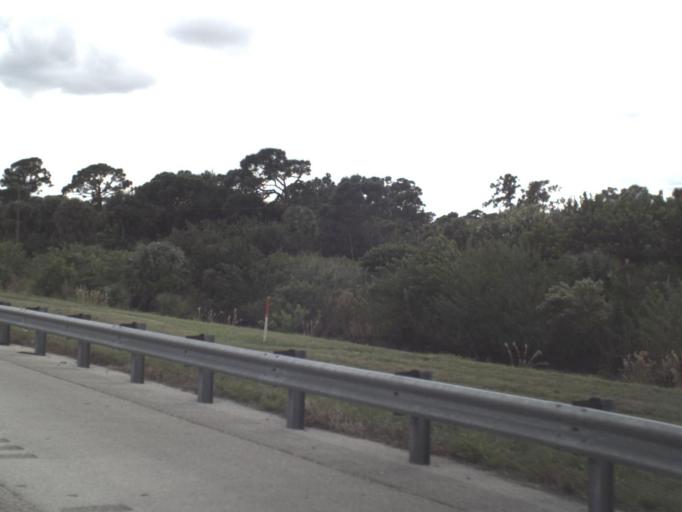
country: US
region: Florida
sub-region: Saint Lucie County
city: Port Saint Lucie
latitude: 27.3061
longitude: -80.3744
